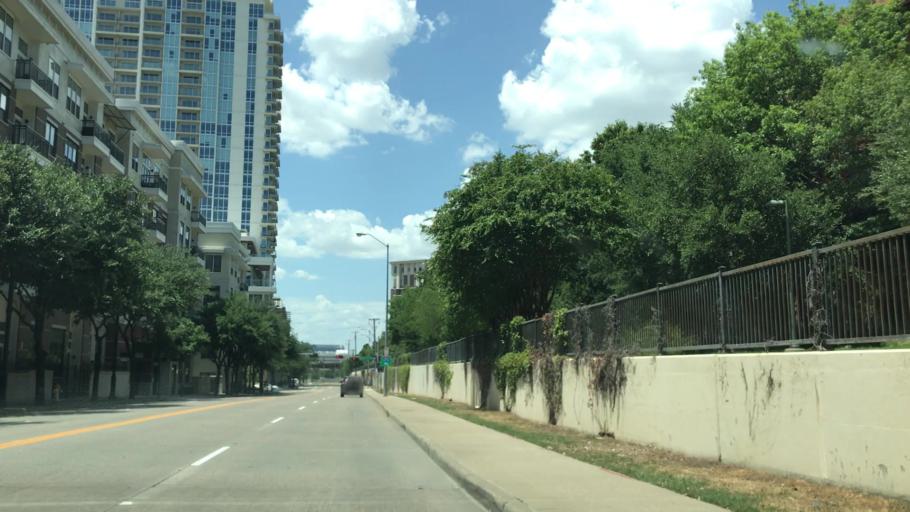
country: US
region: Texas
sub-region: Dallas County
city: Dallas
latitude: 32.7929
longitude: -96.8115
